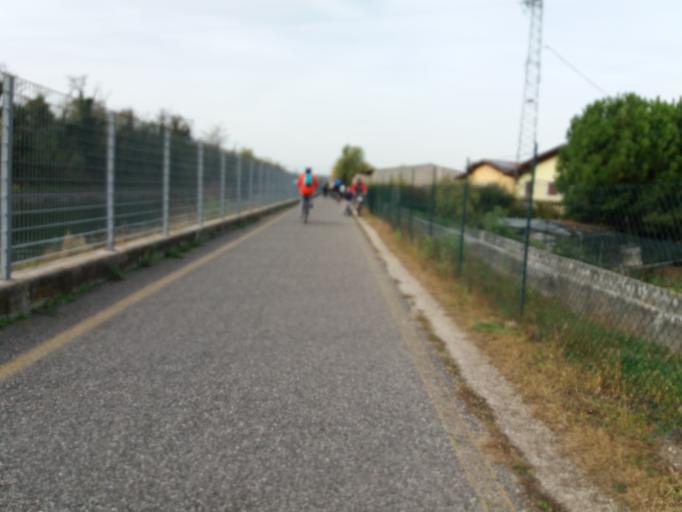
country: IT
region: Veneto
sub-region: Provincia di Verona
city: San Vito al Mantico
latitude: 45.4712
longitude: 10.8838
